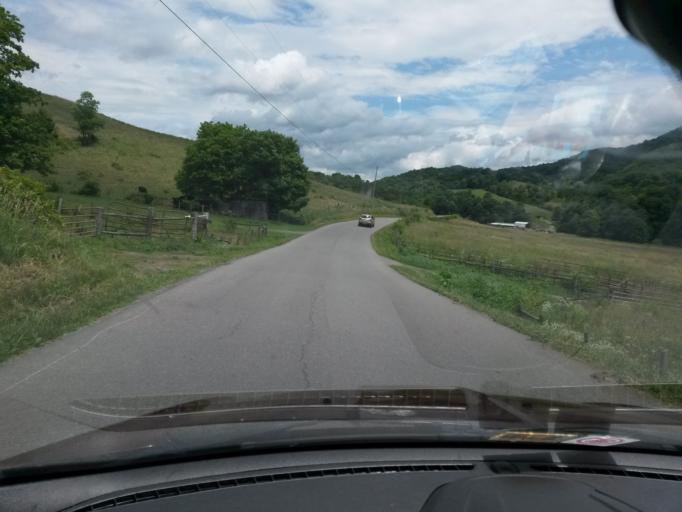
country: US
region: West Virginia
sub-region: Monroe County
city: Union
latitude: 37.5018
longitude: -80.5894
